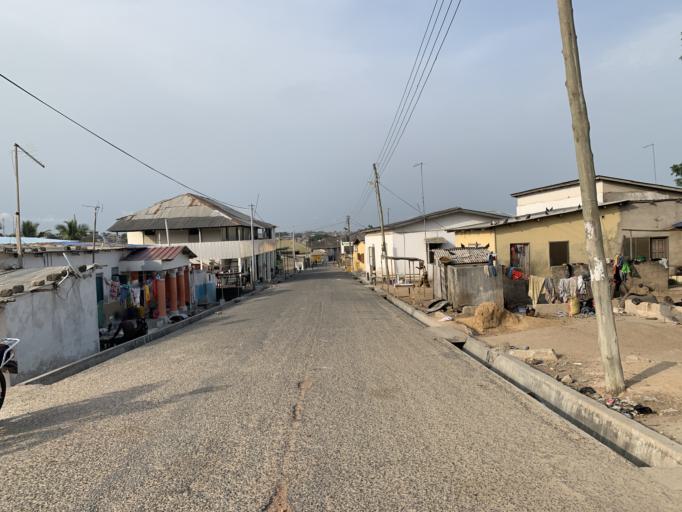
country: GH
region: Central
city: Winneba
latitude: 5.3376
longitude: -0.6226
